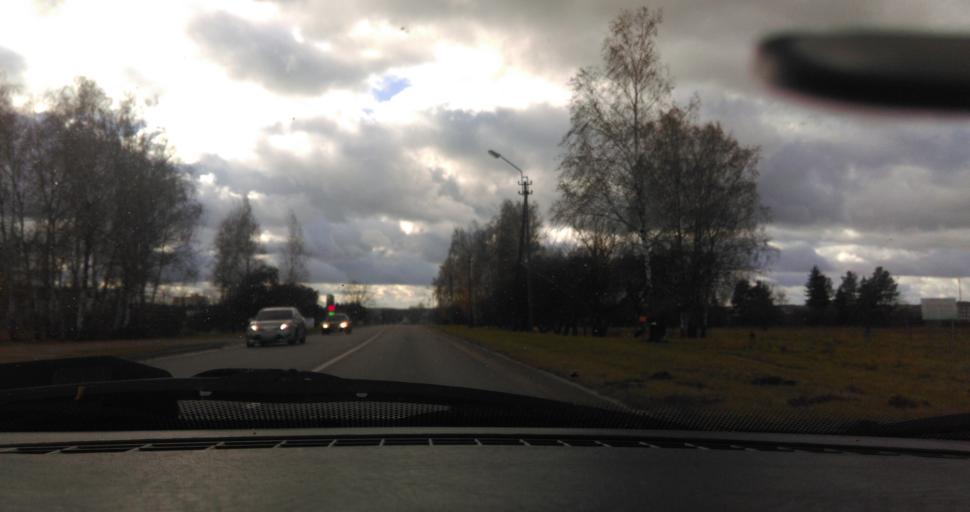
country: LT
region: Utenos apskritis
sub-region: Utena
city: Utena
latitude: 55.5064
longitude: 25.6271
